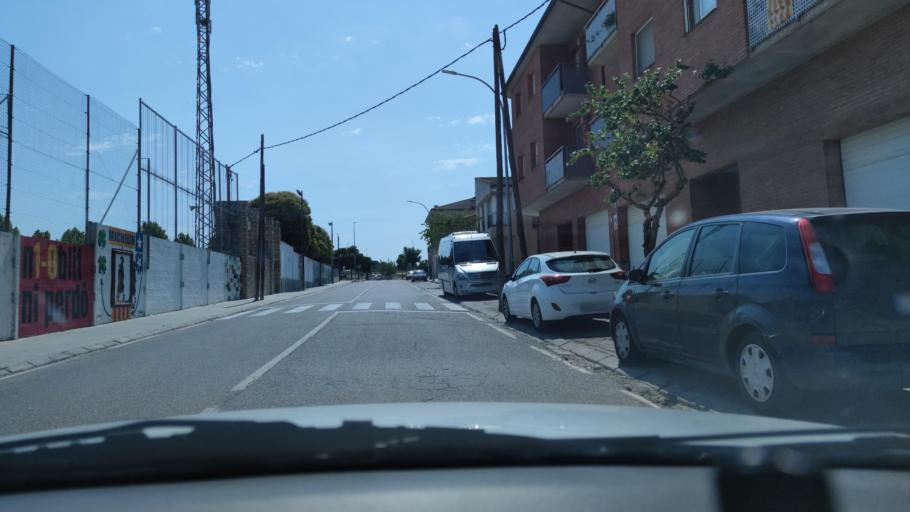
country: ES
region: Catalonia
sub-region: Provincia de Lleida
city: Ivorra
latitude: 41.7840
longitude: 1.2948
